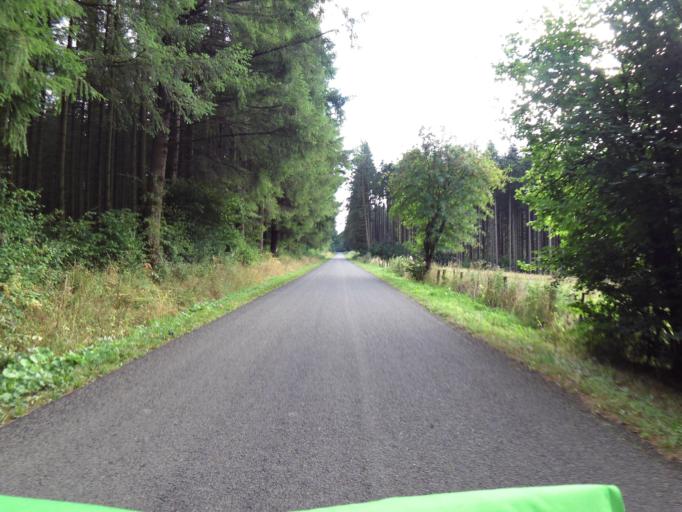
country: BE
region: Wallonia
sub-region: Province de Namur
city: Bievre
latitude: 49.9270
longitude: 5.0098
